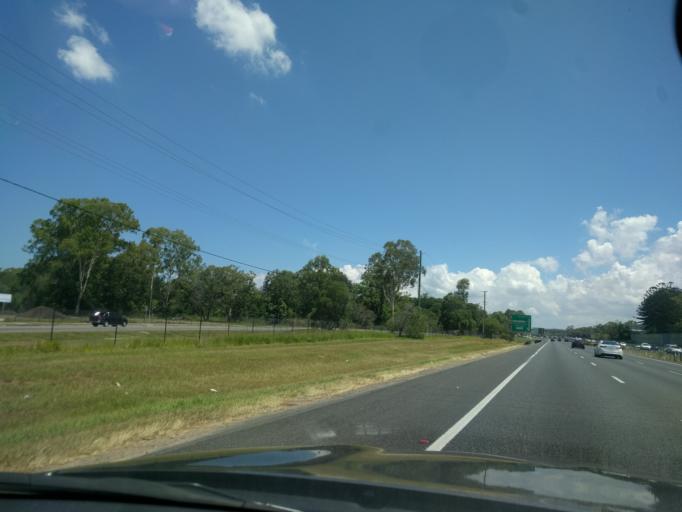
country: AU
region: Queensland
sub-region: Moreton Bay
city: Burpengary
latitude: -27.1486
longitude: 152.9782
